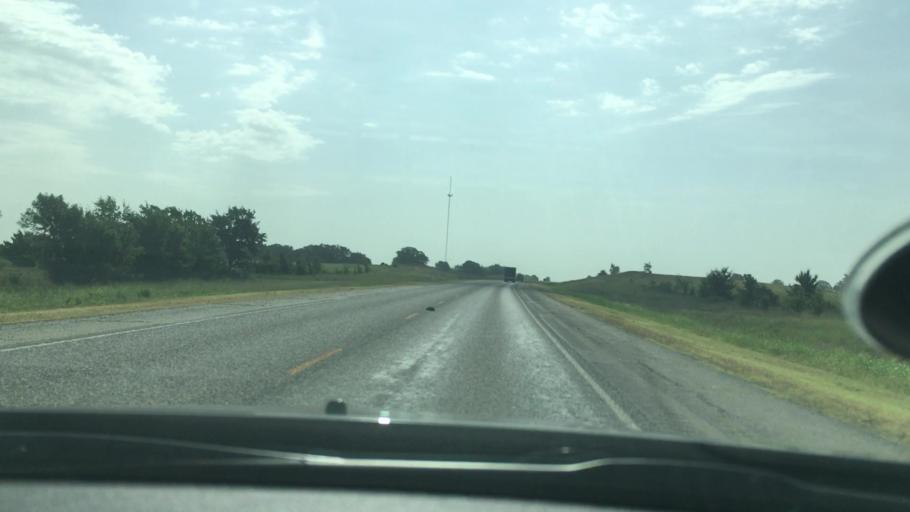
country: US
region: Oklahoma
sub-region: Coal County
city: Coalgate
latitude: 34.5995
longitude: -96.3209
